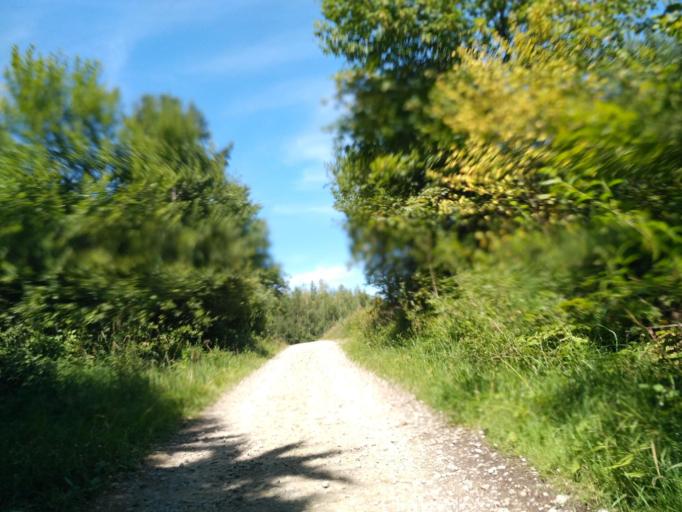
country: PL
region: Subcarpathian Voivodeship
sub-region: Powiat sanocki
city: Bukowsko
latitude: 49.4854
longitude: 22.0936
